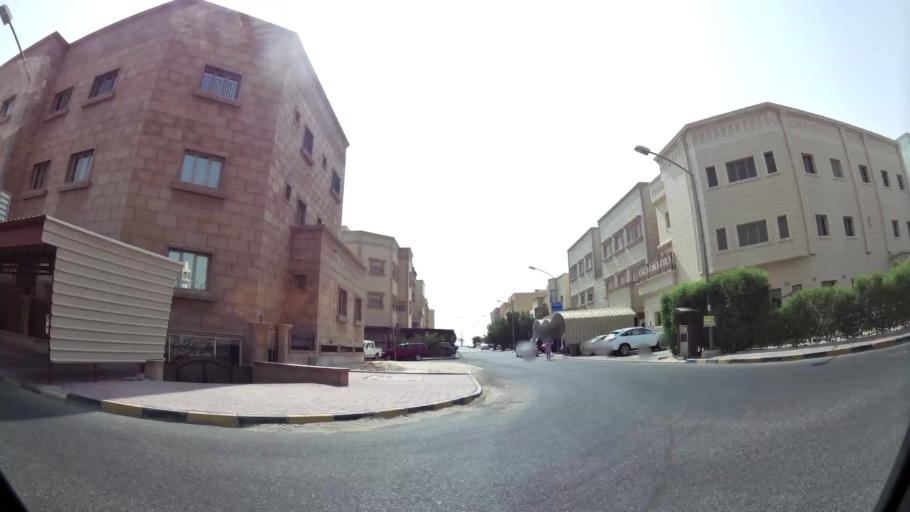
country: KW
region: Muhafazat al Jahra'
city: Al Jahra'
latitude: 29.3039
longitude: 47.7012
